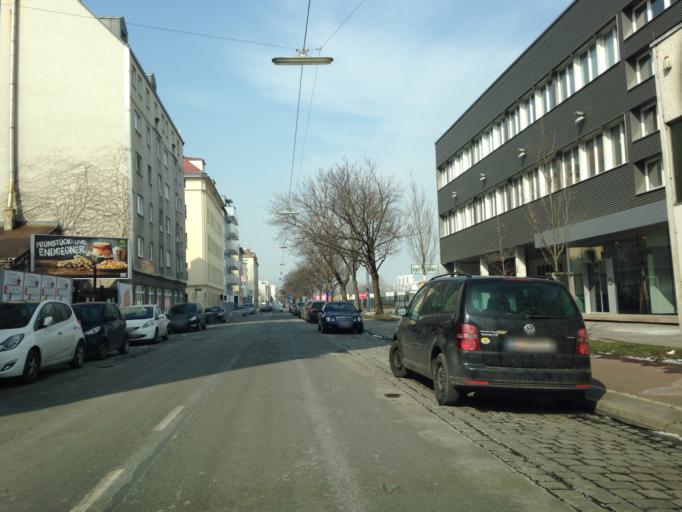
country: AT
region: Vienna
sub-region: Wien Stadt
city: Vienna
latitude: 48.2290
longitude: 16.3803
